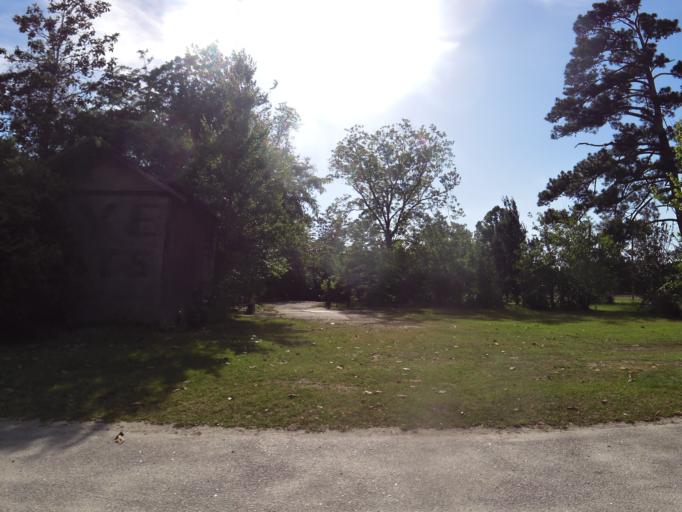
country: US
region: South Carolina
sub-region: Allendale County
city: Fairfax
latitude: 32.8595
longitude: -81.2381
